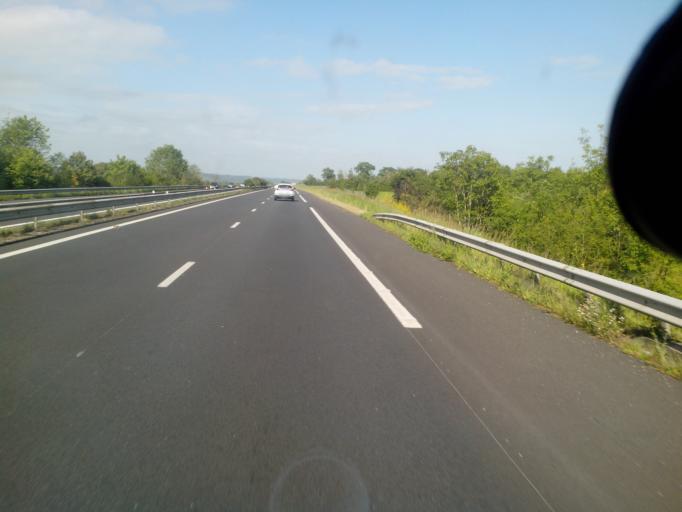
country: FR
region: Lower Normandy
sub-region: Departement du Calvados
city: Bavent
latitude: 49.2129
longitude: -0.1383
